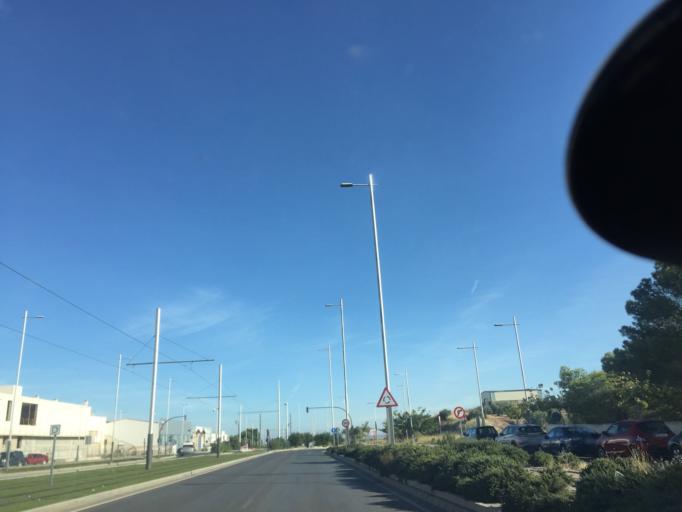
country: ES
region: Andalusia
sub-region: Provincia de Jaen
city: Jaen
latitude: 37.7962
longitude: -3.7794
